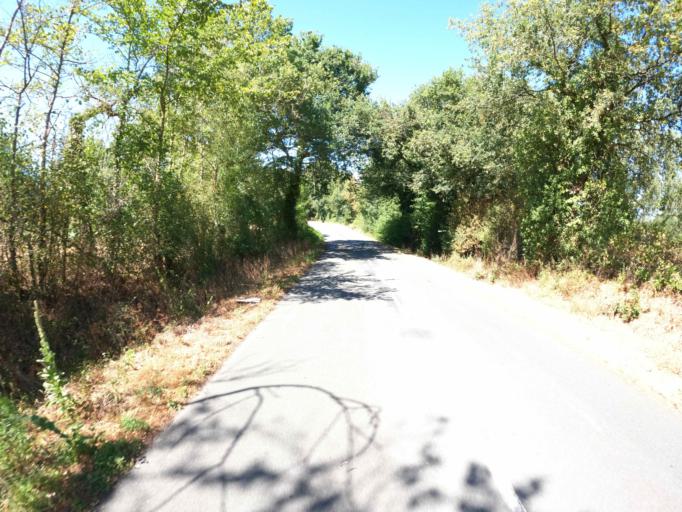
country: FR
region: Pays de la Loire
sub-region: Departement de la Vendee
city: Saint-Aubin-des-Ormeaux
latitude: 46.9872
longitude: -1.0477
